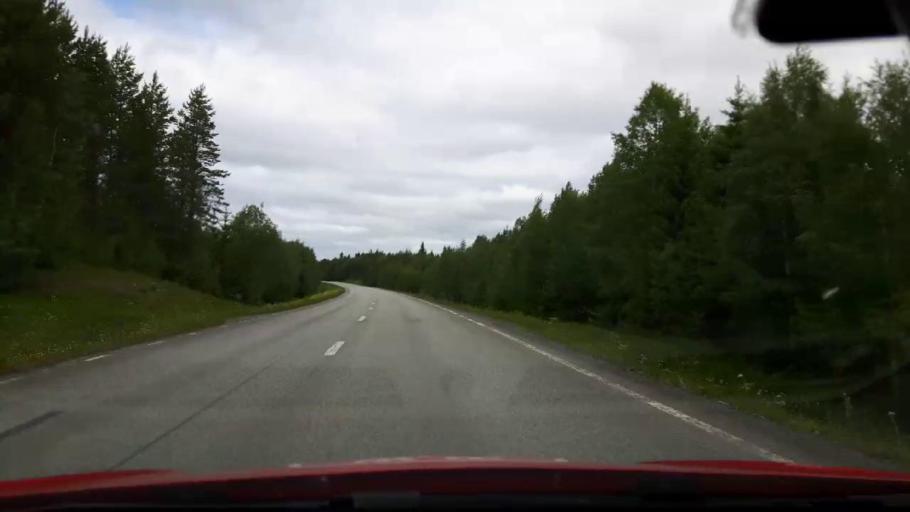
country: SE
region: Jaemtland
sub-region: Krokoms Kommun
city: Krokom
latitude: 63.3838
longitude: 14.5076
